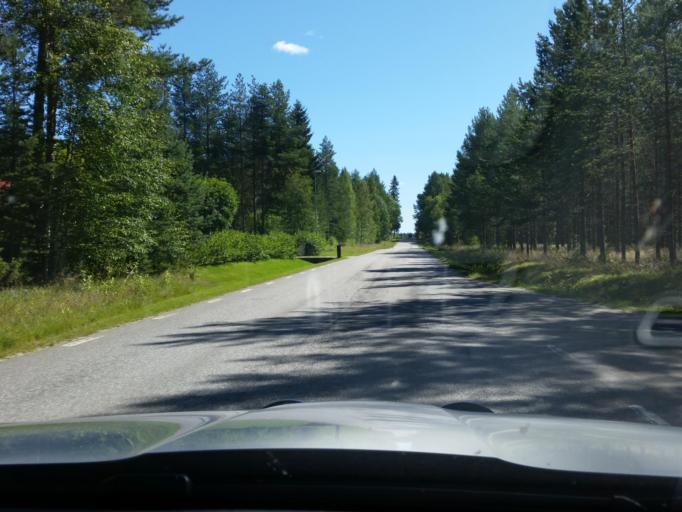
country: SE
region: Norrbotten
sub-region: Pitea Kommun
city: Bergsviken
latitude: 65.3093
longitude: 21.3592
